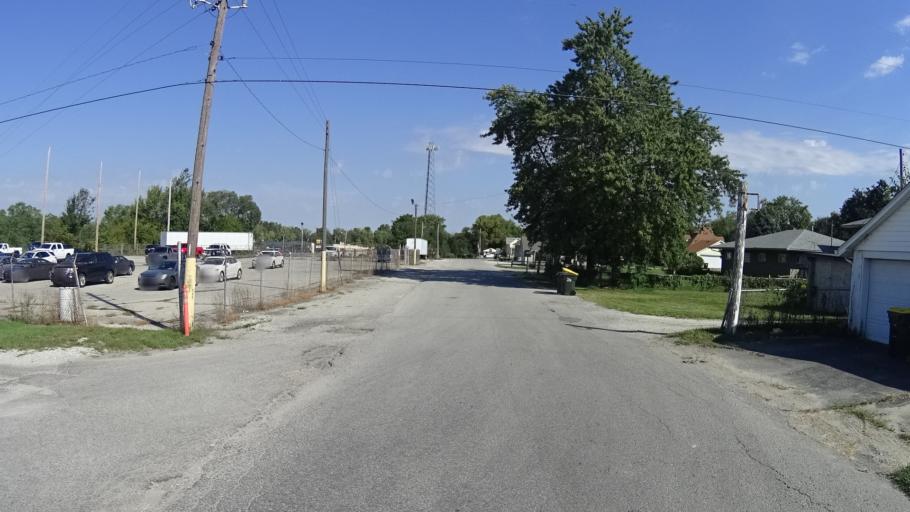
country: US
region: Indiana
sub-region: Madison County
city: Lapel
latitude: 40.0679
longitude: -85.8535
